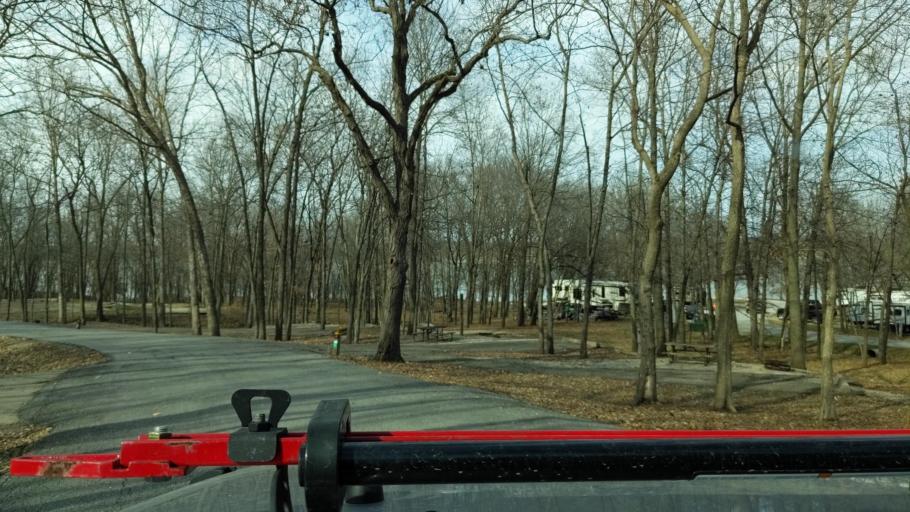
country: US
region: Missouri
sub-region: Macon County
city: Macon
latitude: 39.7709
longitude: -92.5222
